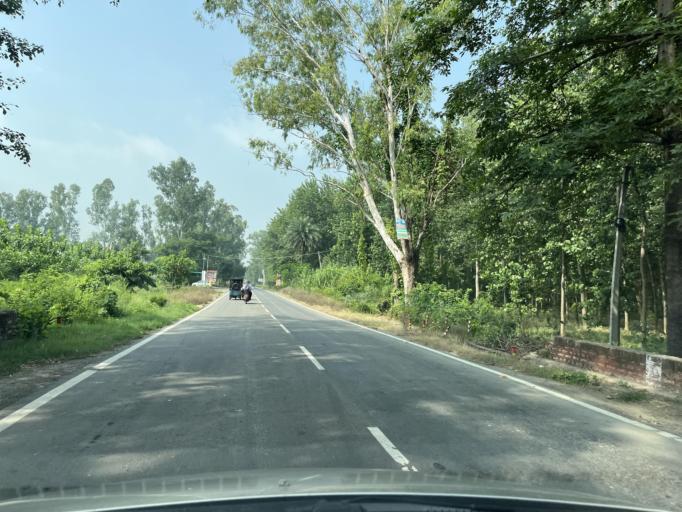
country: IN
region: Uttarakhand
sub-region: Udham Singh Nagar
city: Bazpur
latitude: 29.1772
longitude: 79.1742
